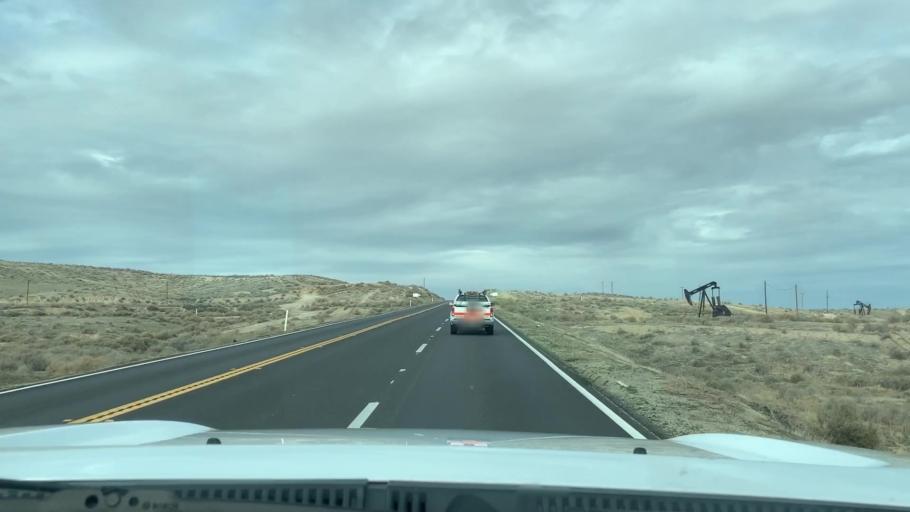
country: US
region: California
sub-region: Kern County
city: South Taft
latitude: 35.1158
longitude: -119.4301
